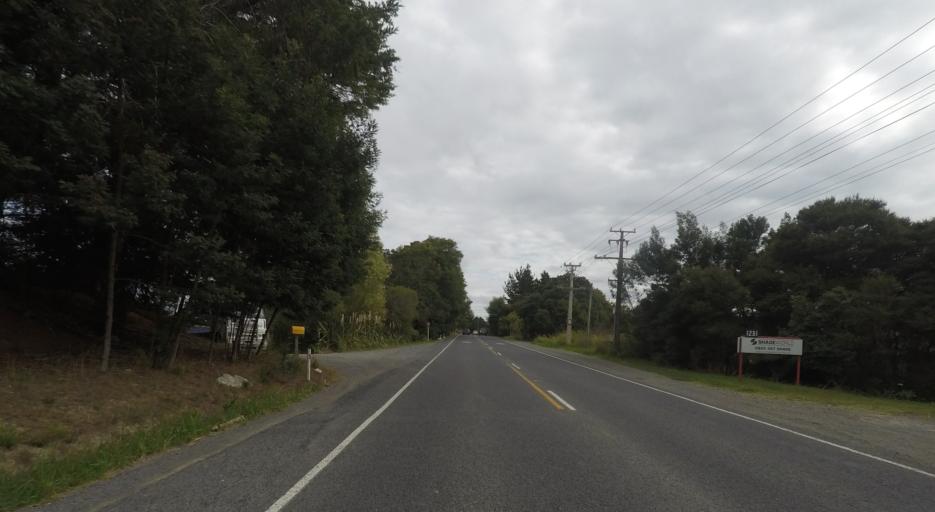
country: NZ
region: Auckland
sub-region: Auckland
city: Rothesay Bay
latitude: -36.6937
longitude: 174.7074
